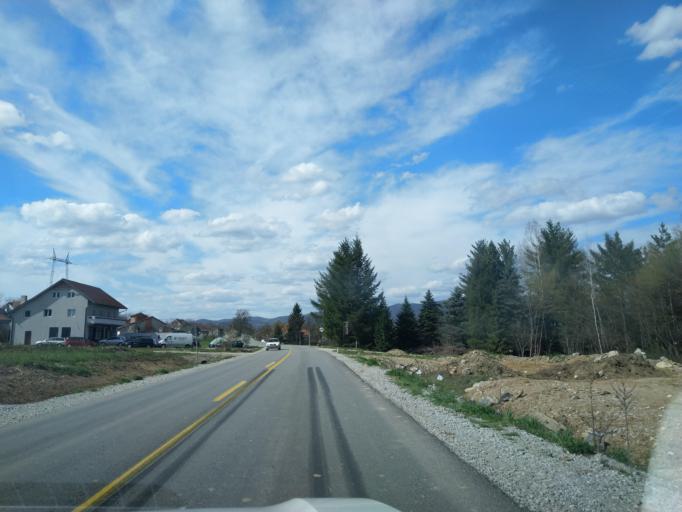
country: RS
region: Central Serbia
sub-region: Zlatiborski Okrug
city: Pozega
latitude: 43.8186
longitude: 20.0861
